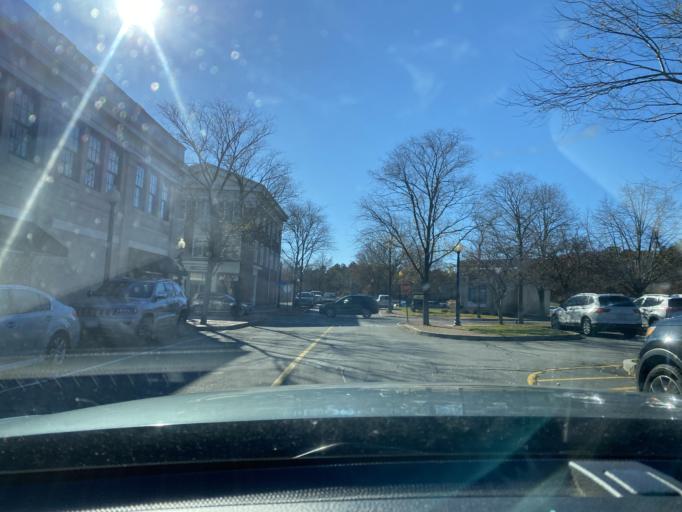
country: US
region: Massachusetts
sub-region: Barnstable County
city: Mashpee
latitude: 41.6173
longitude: -70.4918
